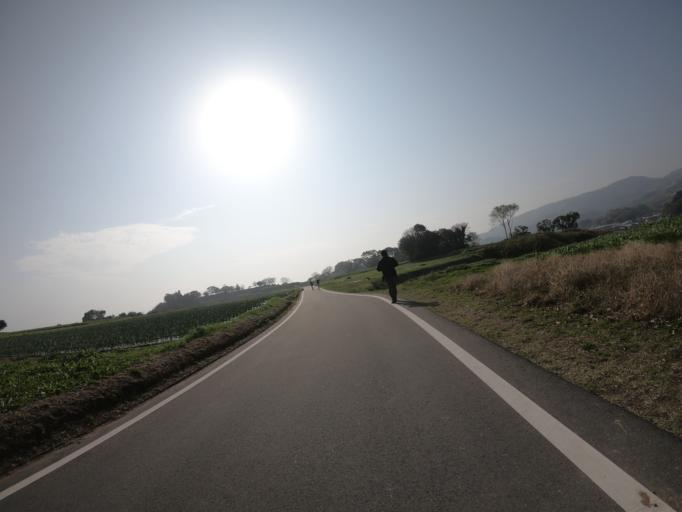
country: JP
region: Nagasaki
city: Shimabara
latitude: 32.6325
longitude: 130.2555
